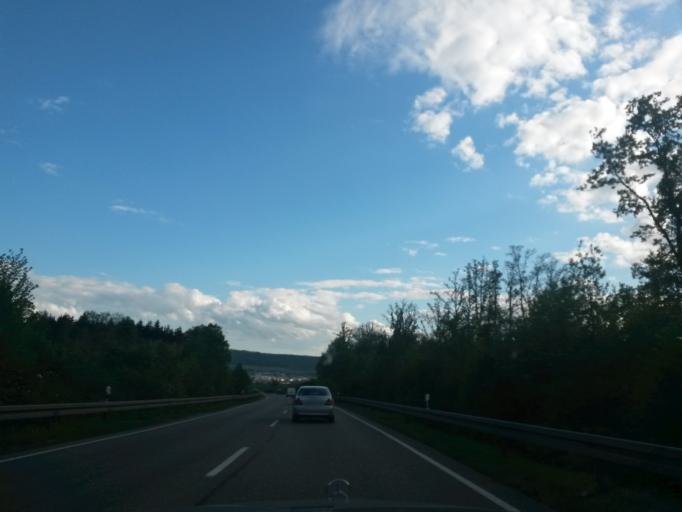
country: DE
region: Baden-Wuerttemberg
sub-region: Regierungsbezirk Stuttgart
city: Aalen
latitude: 48.8549
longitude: 10.0704
